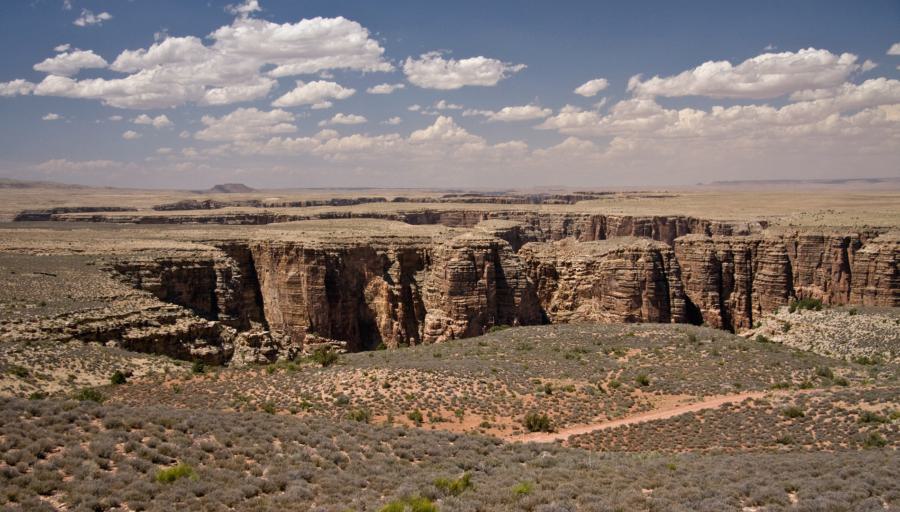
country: US
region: Arizona
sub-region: Coconino County
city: Tuba City
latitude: 35.9394
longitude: -111.6677
